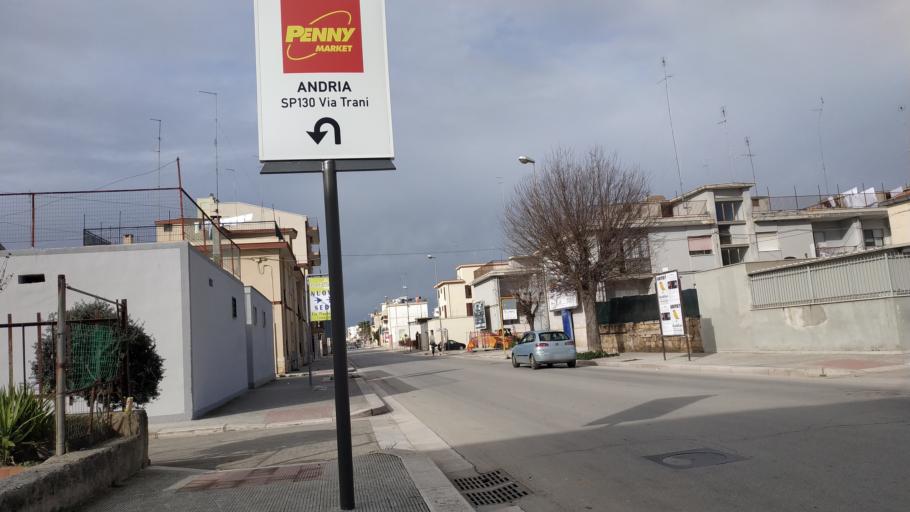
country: IT
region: Apulia
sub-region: Provincia di Barletta - Andria - Trani
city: Andria
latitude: 41.2390
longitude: 16.2986
